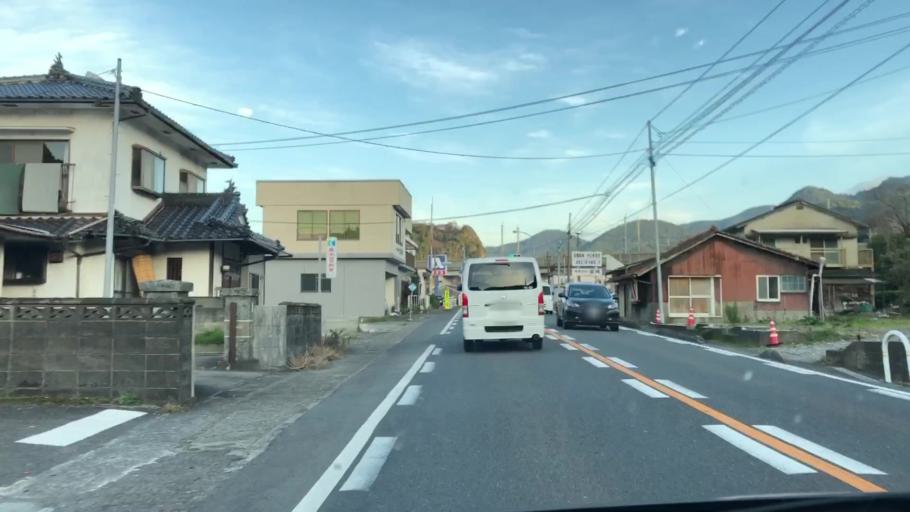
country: JP
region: Kumamoto
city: Minamata
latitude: 32.2334
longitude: 130.4491
